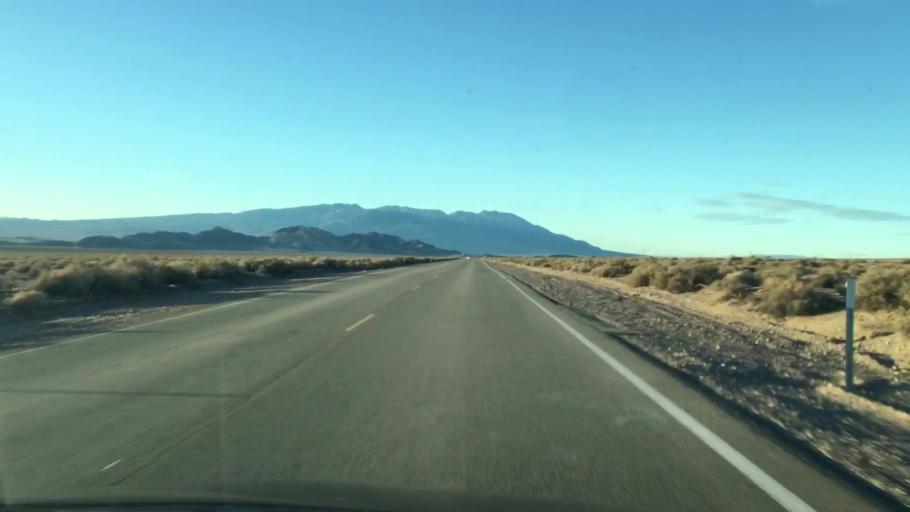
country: US
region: California
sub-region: San Bernardino County
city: Fort Irwin
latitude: 35.3509
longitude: -116.0909
